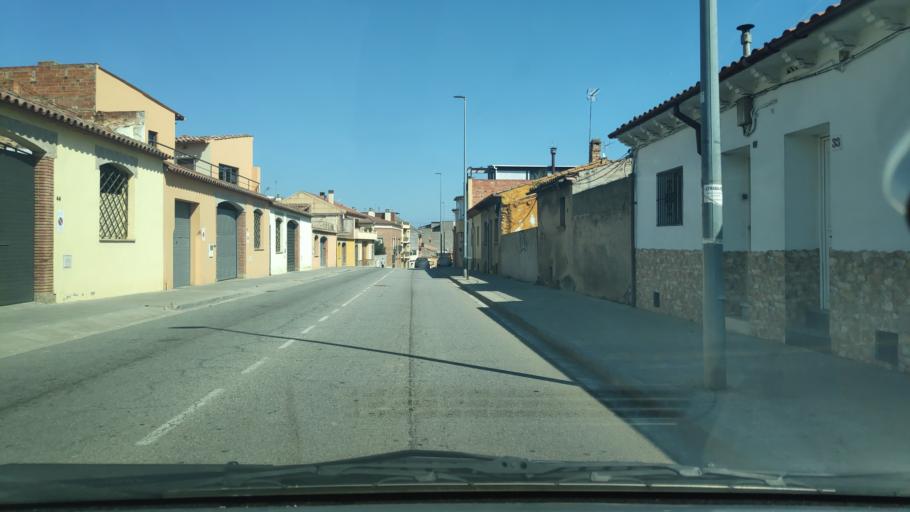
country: ES
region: Catalonia
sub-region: Provincia de Barcelona
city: Santa Perpetua de Mogoda
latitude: 41.5349
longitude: 2.1766
